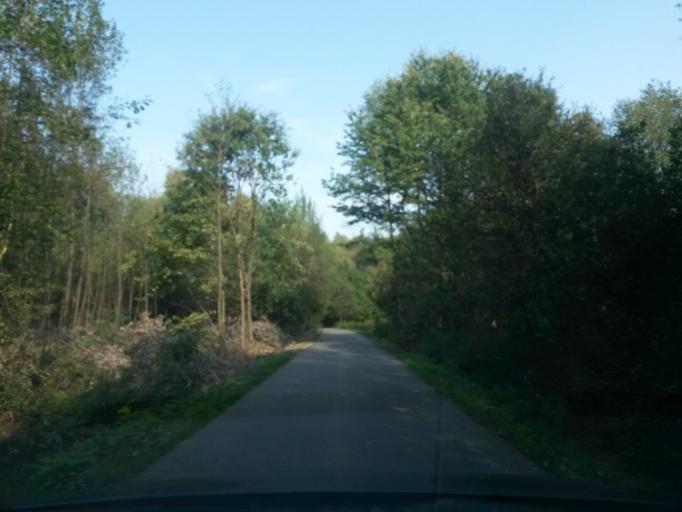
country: PL
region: Subcarpathian Voivodeship
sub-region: Powiat debicki
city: Leki Gorne
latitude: 49.9871
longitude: 21.1484
